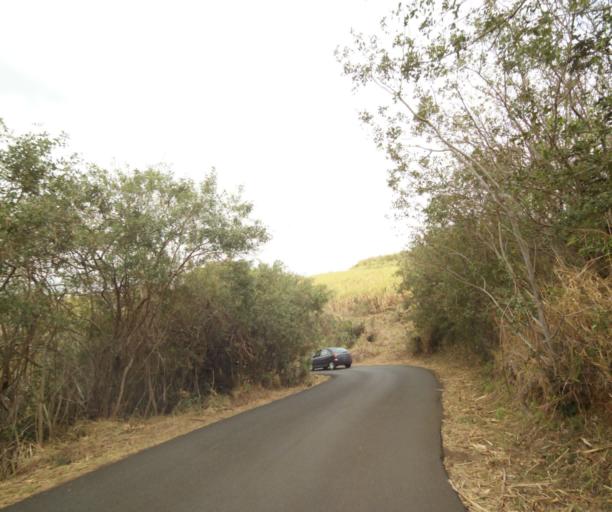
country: RE
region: Reunion
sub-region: Reunion
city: Saint-Paul
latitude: -21.0266
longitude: 55.3036
